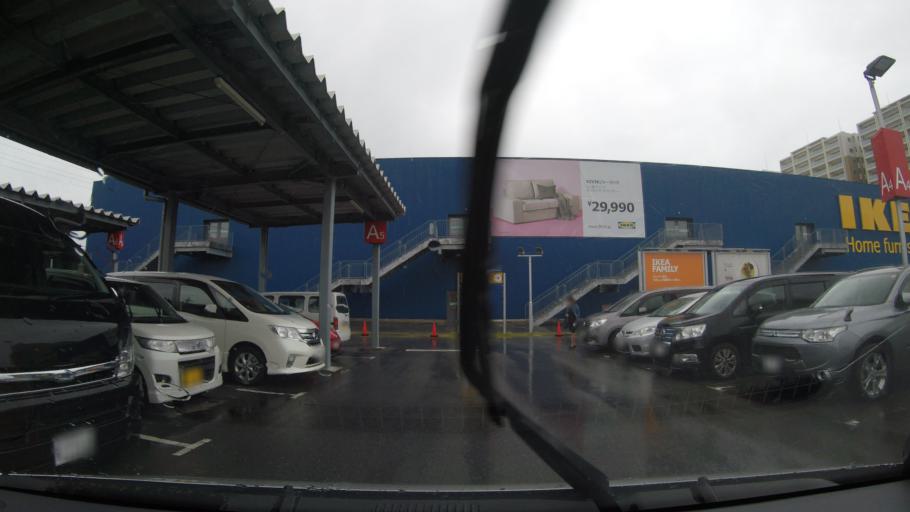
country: JP
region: Fukuoka
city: Shingu
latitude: 33.7095
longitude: 130.4508
